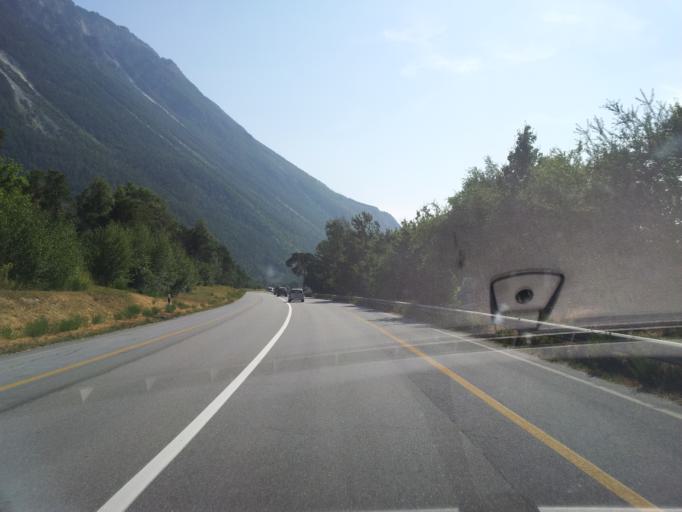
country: CH
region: Valais
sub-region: Leuk District
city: Varen
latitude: 46.3064
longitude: 7.6105
